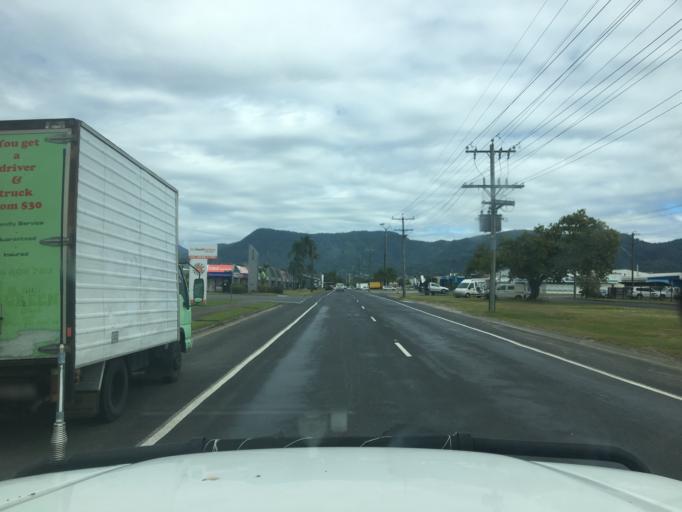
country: AU
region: Queensland
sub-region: Cairns
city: Woree
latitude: -16.9400
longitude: 145.7612
